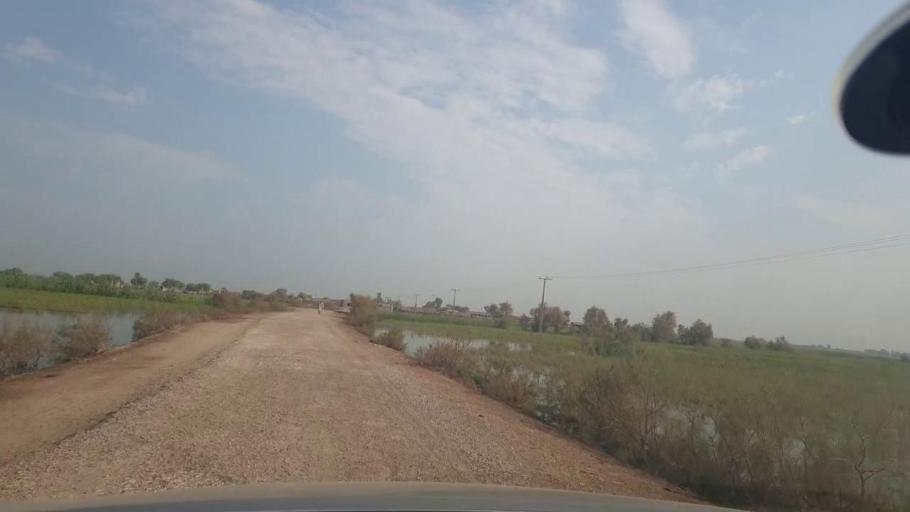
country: PK
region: Balochistan
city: Mehrabpur
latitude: 28.0702
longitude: 68.2109
